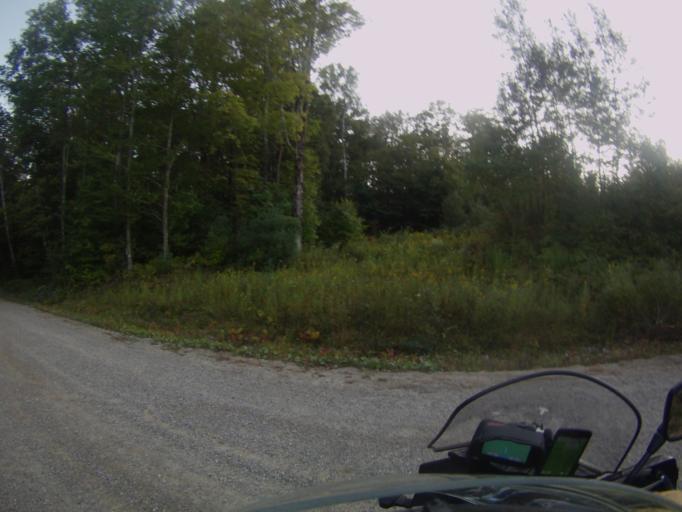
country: US
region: Vermont
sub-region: Addison County
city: Middlebury (village)
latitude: 43.9982
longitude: -73.0448
